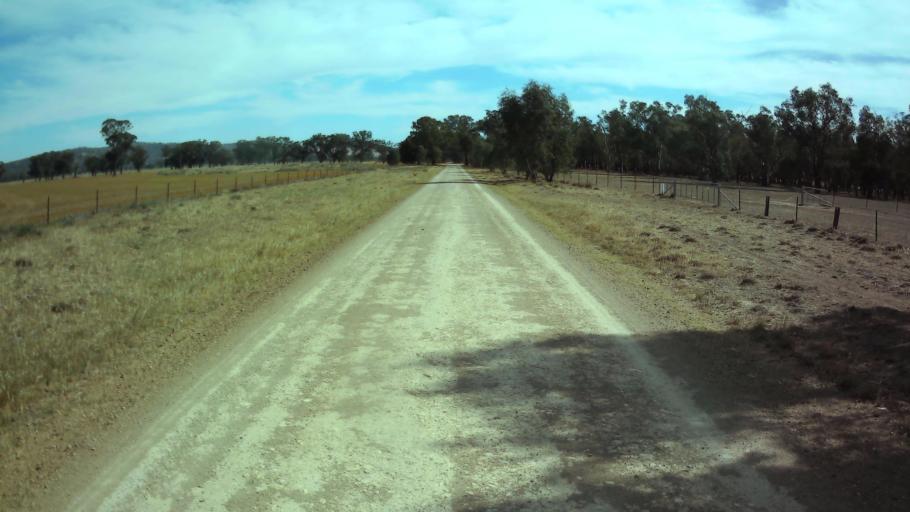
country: AU
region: New South Wales
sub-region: Weddin
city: Grenfell
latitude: -33.7047
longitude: 148.3015
